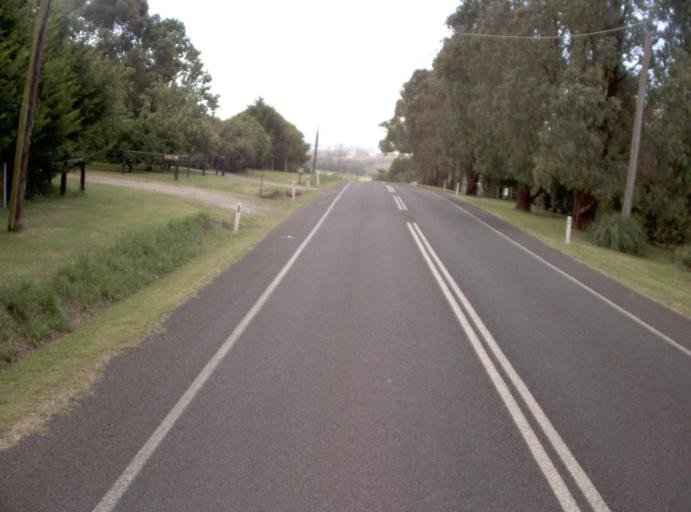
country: AU
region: Victoria
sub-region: Baw Baw
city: Warragul
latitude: -38.0961
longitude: 145.9212
